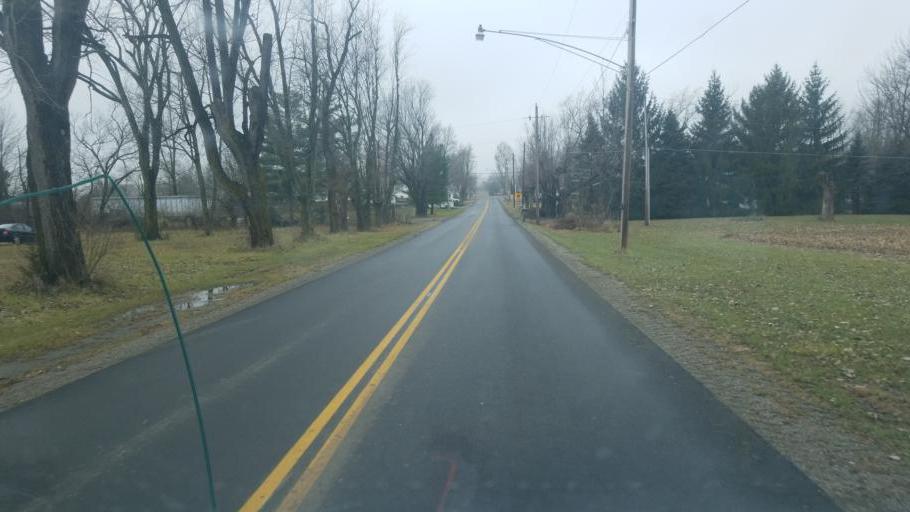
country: US
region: Ohio
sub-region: Champaign County
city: North Lewisburg
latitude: 40.2907
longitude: -83.5801
